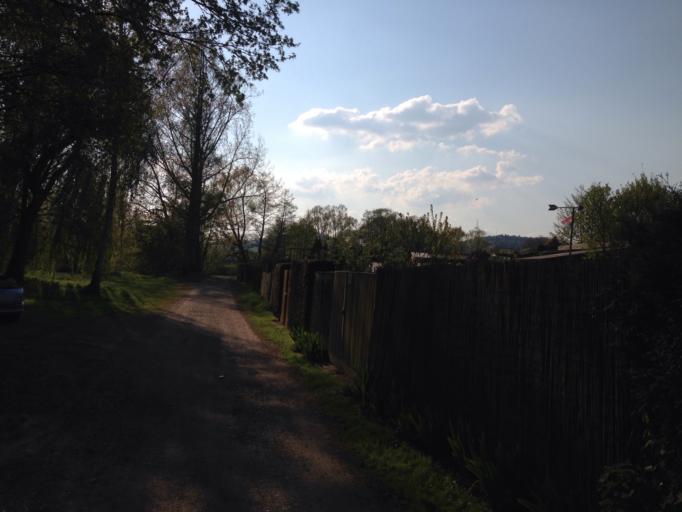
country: DE
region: Hesse
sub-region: Regierungsbezirk Giessen
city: Giessen
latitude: 50.6086
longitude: 8.6711
